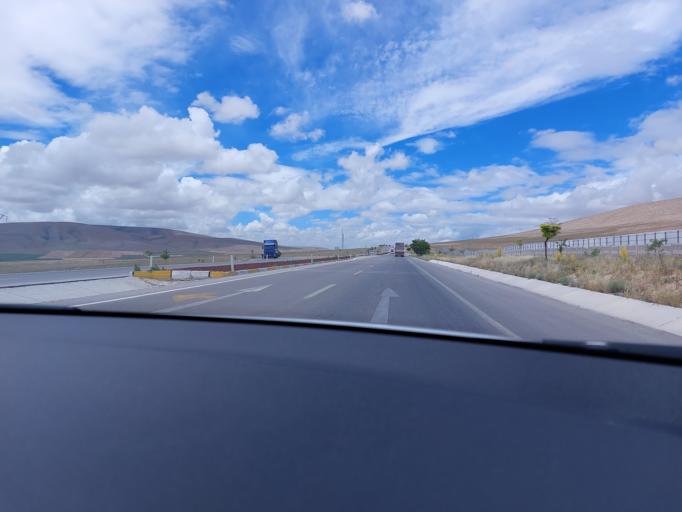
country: TR
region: Konya
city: Obruk
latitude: 38.0617
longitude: 33.0488
